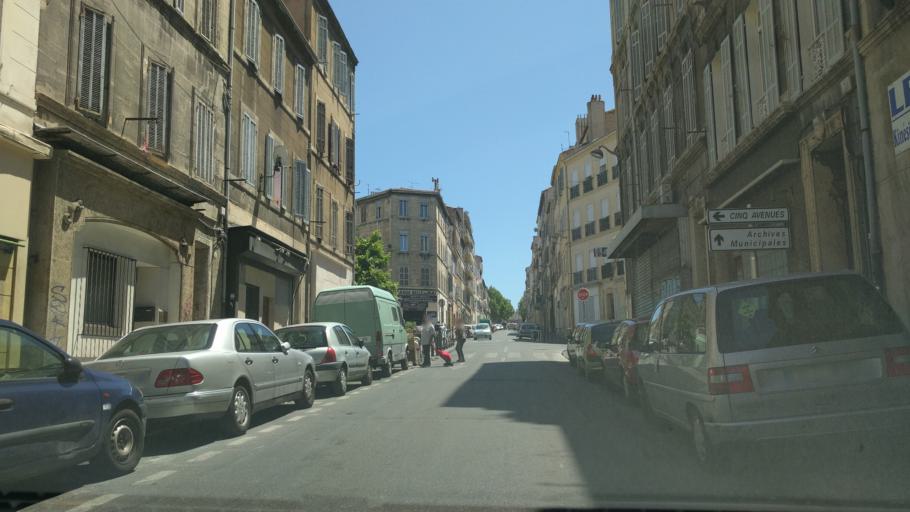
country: FR
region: Provence-Alpes-Cote d'Azur
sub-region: Departement des Bouches-du-Rhone
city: Marseille 03
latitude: 43.3106
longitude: 5.3851
